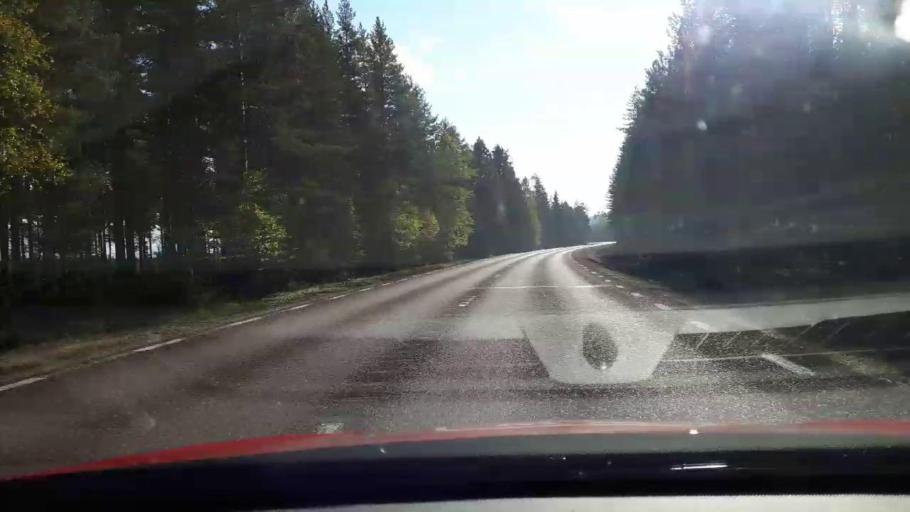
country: SE
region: Gaevleborg
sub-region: Ljusdals Kommun
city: Farila
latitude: 61.9049
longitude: 15.6360
